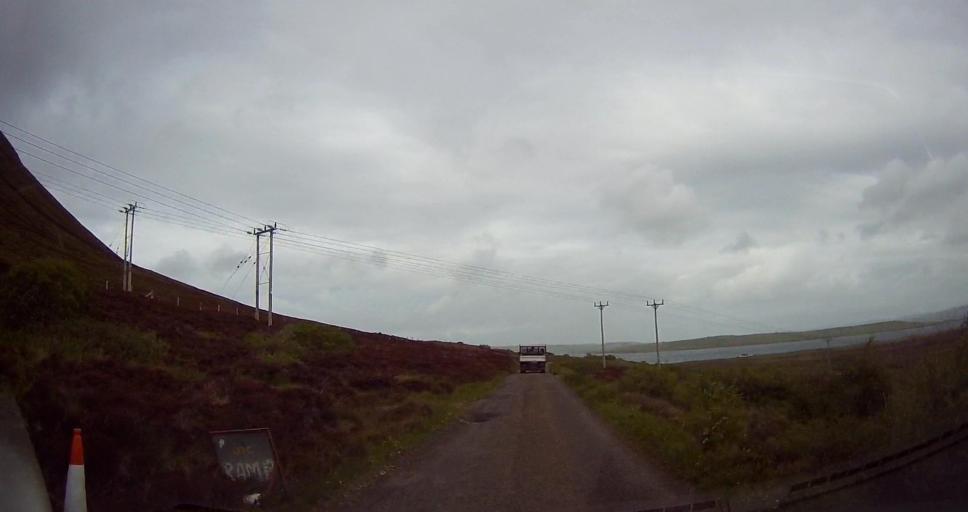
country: GB
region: Scotland
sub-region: Orkney Islands
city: Stromness
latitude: 58.8959
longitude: -3.3145
